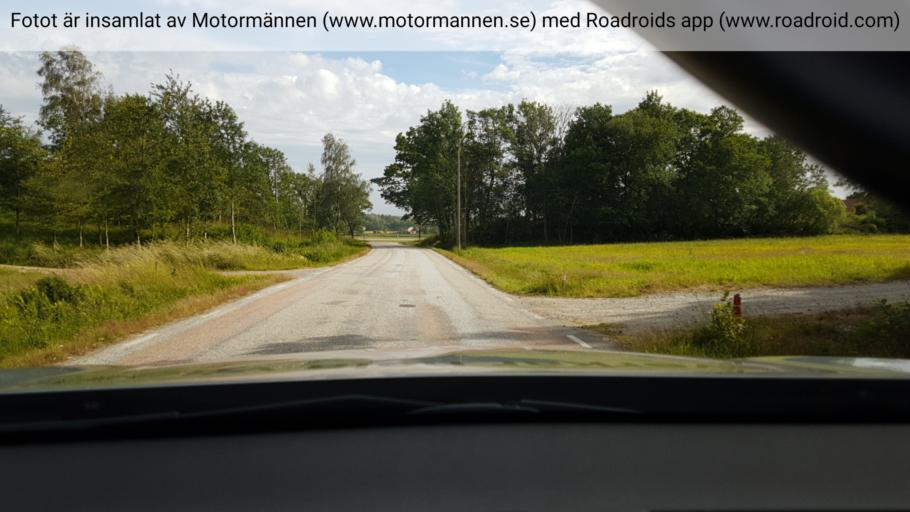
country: SE
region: Vaestra Goetaland
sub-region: Orust
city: Henan
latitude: 58.1362
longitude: 11.6582
